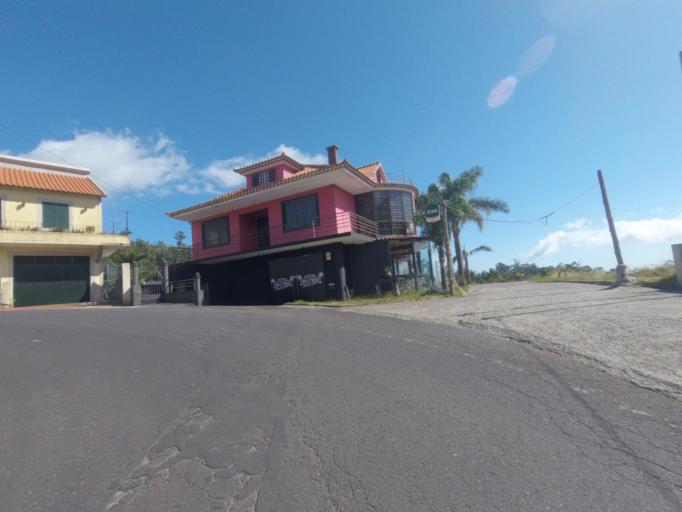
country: PT
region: Madeira
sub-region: Ribeira Brava
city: Campanario
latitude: 32.6935
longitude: -17.0181
